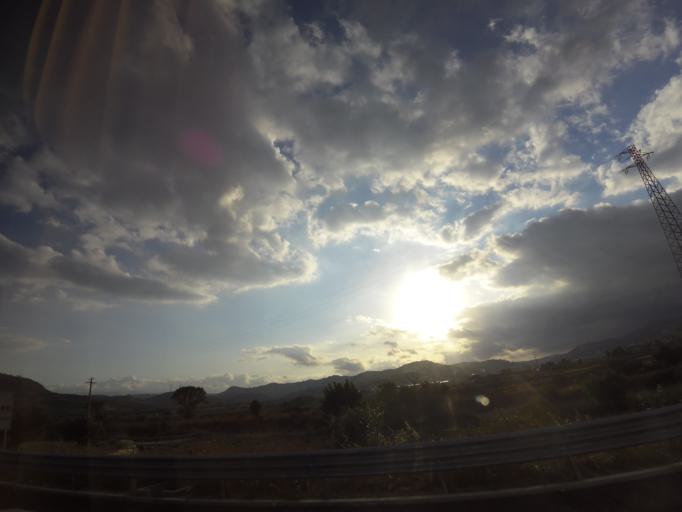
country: IT
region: Calabria
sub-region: Provincia di Catanzaro
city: Catanzaro
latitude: 38.8861
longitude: 16.5560
